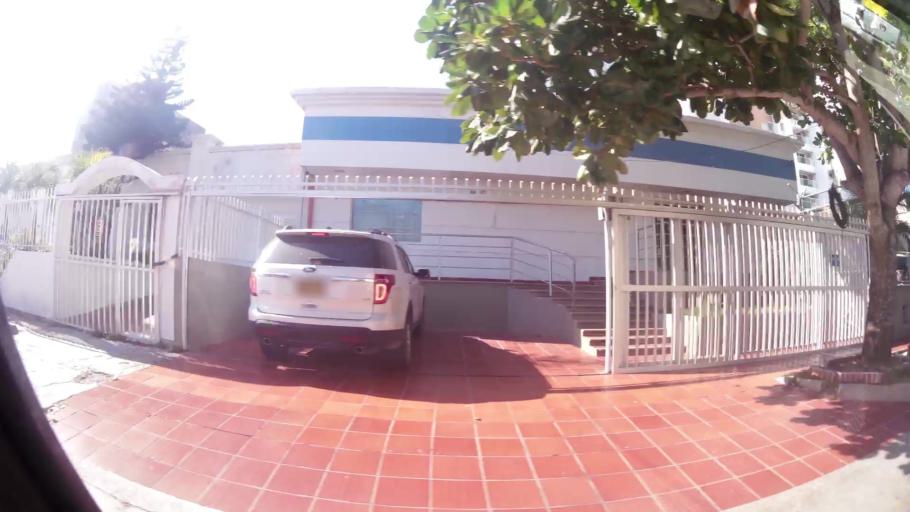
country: CO
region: Atlantico
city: Barranquilla
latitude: 11.0034
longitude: -74.8258
